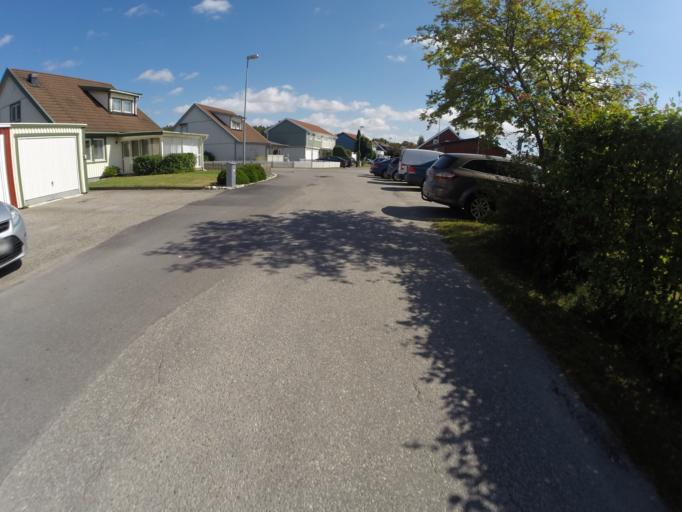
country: SE
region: Soedermanland
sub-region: Eskilstuna Kommun
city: Torshalla
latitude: 59.4078
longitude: 16.4885
